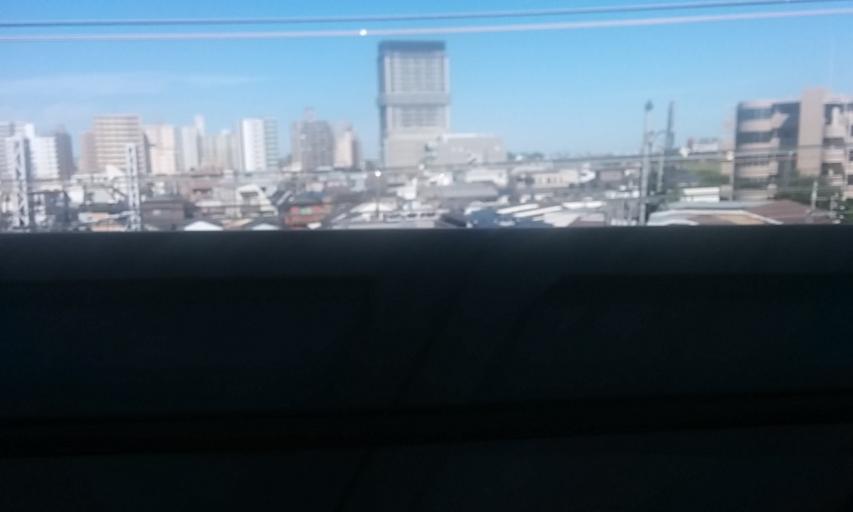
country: JP
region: Saitama
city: Soka
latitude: 35.7544
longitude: 139.8067
